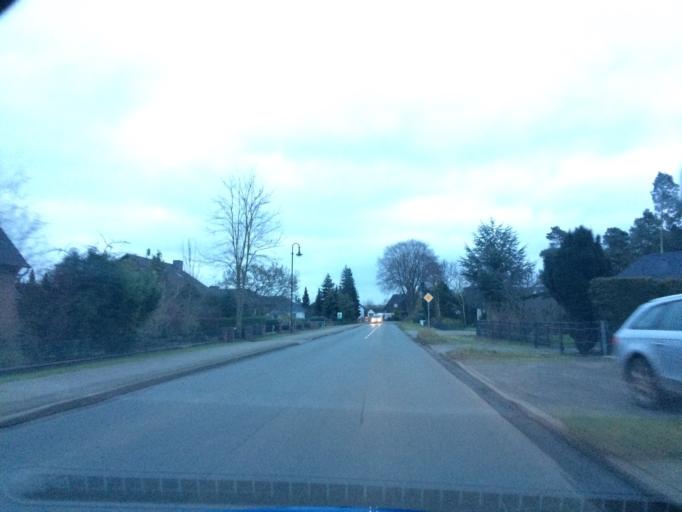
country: DE
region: Lower Saxony
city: Vogelsen
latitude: 53.2922
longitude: 10.3598
